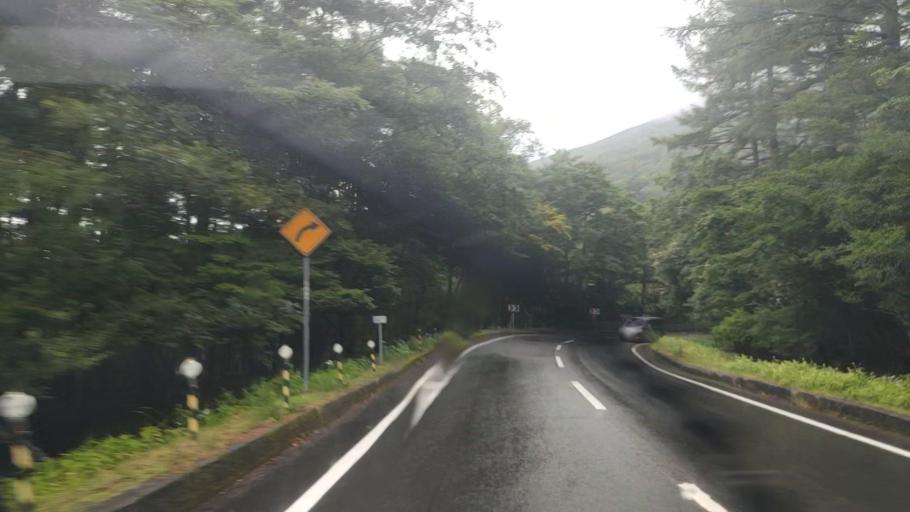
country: JP
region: Shizuoka
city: Fujinomiya
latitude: 35.3244
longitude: 138.7199
